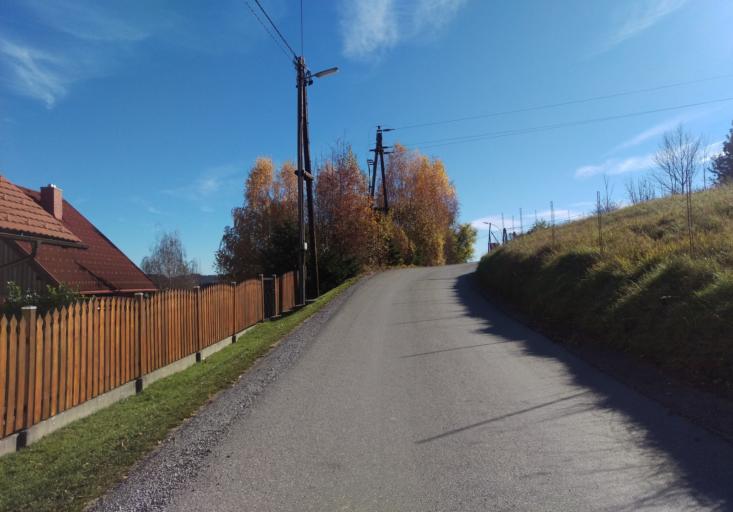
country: AT
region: Styria
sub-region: Graz Stadt
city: Mariatrost
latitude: 47.1251
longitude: 15.4947
